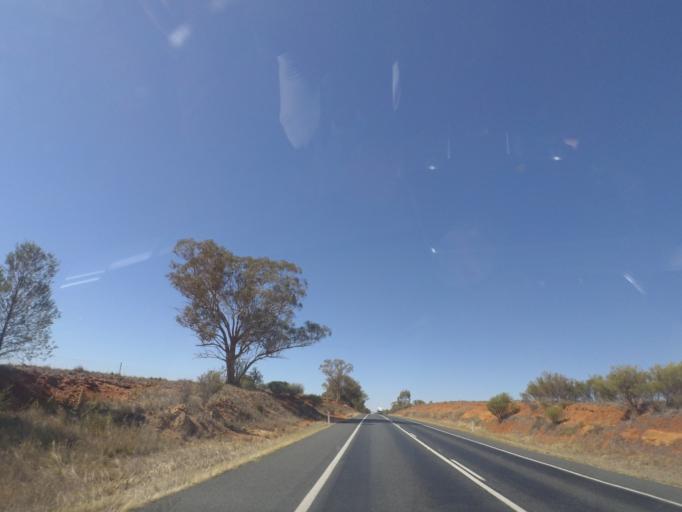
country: AU
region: New South Wales
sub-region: Bland
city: West Wyalong
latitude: -34.1786
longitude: 147.1138
